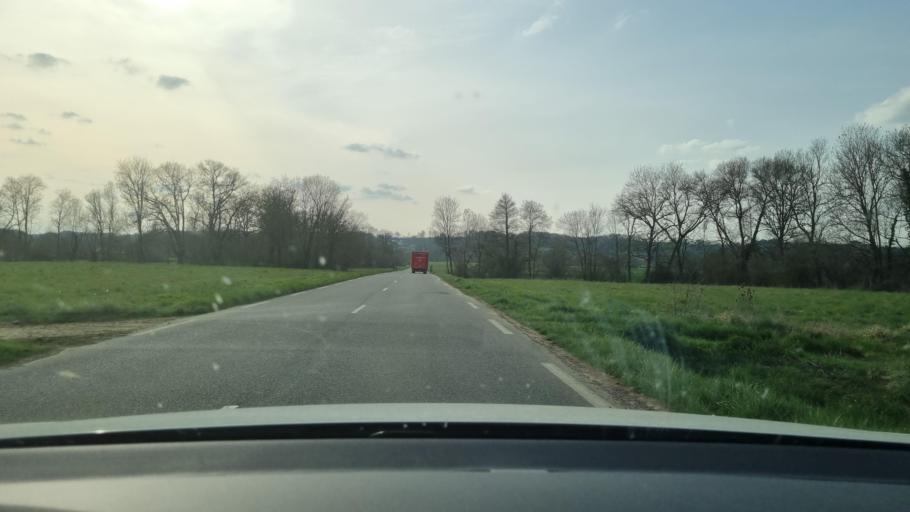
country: FR
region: Aquitaine
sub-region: Departement des Pyrenees-Atlantiques
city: Soumoulou
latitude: 43.3771
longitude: -0.1136
